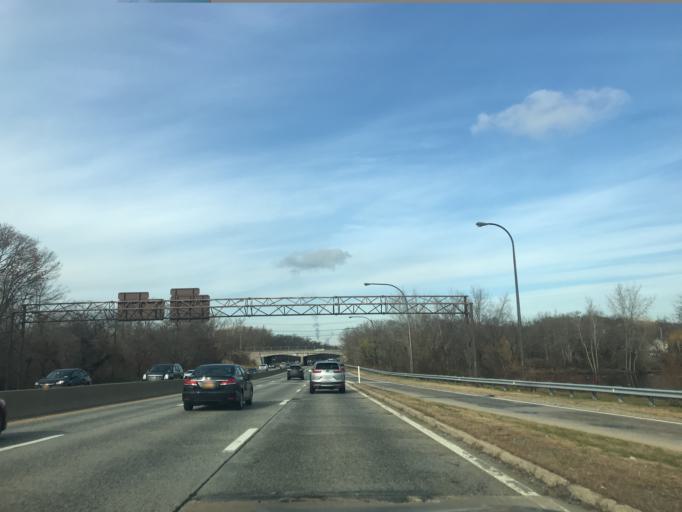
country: US
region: New York
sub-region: Nassau County
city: North Merrick
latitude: 40.6925
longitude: -73.5753
